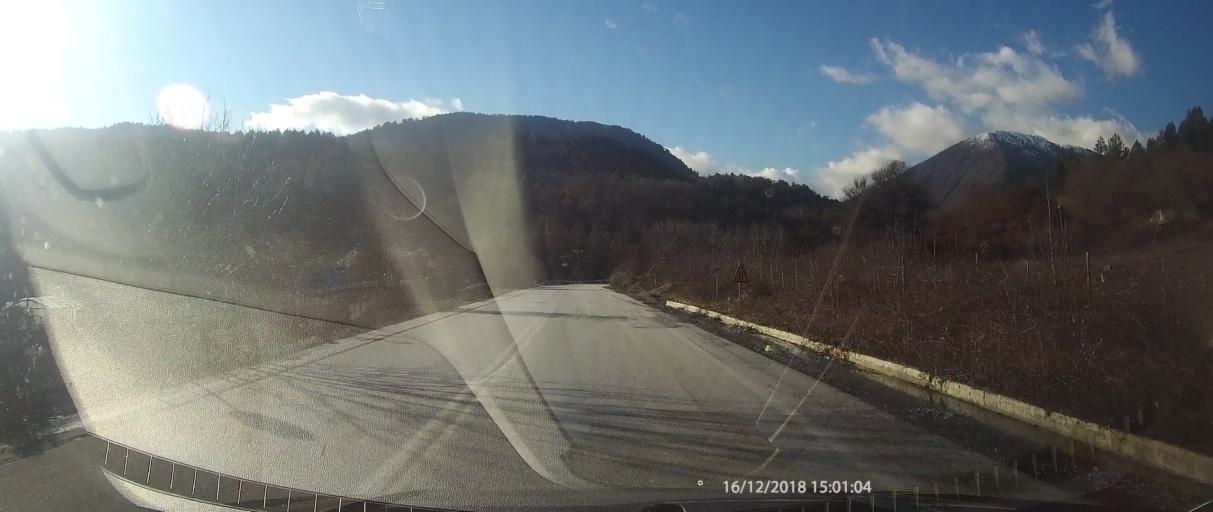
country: GR
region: West Macedonia
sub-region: Nomos Kastorias
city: Nestorio
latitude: 40.2193
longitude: 21.0103
